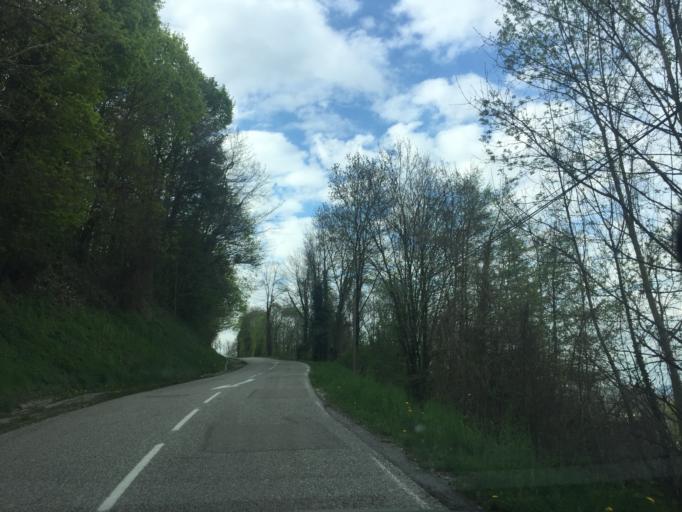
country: FR
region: Rhone-Alpes
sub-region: Departement de la Savoie
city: Cognin
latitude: 45.5672
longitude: 5.8862
